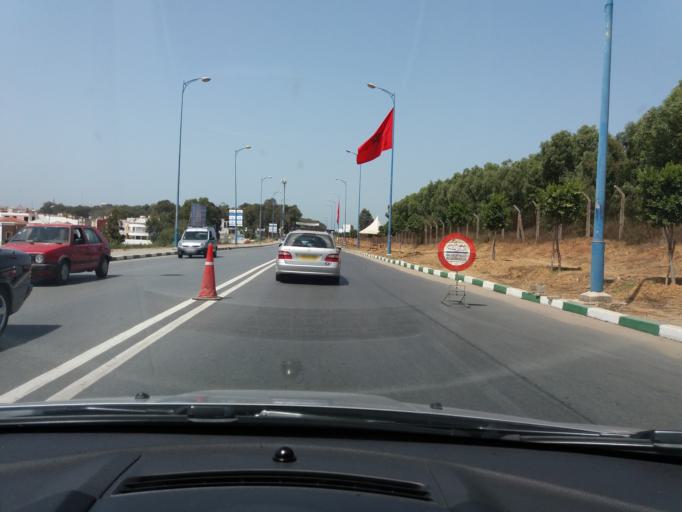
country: MA
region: Gharb-Chrarda-Beni Hssen
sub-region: Kenitra Province
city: Kenitra
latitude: 34.2705
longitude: -6.6381
